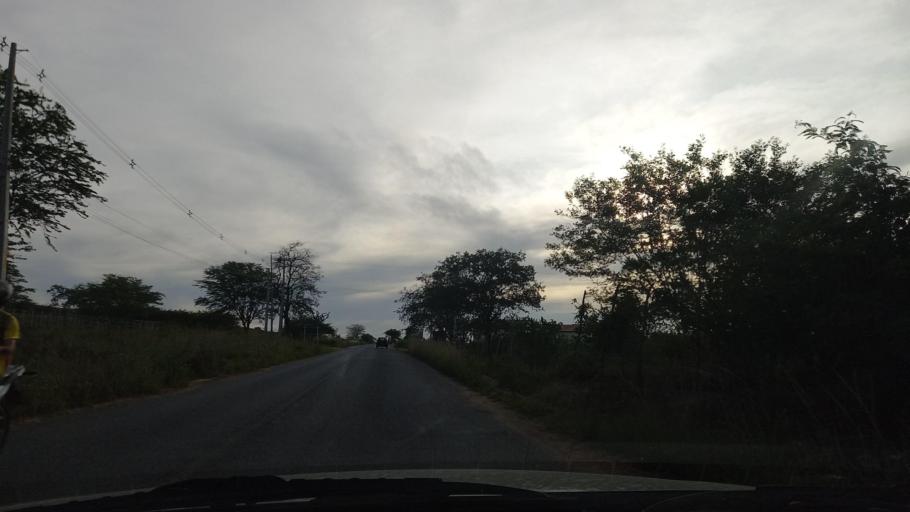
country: BR
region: Pernambuco
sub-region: Bezerros
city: Bezerros
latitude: -8.2171
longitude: -35.7457
